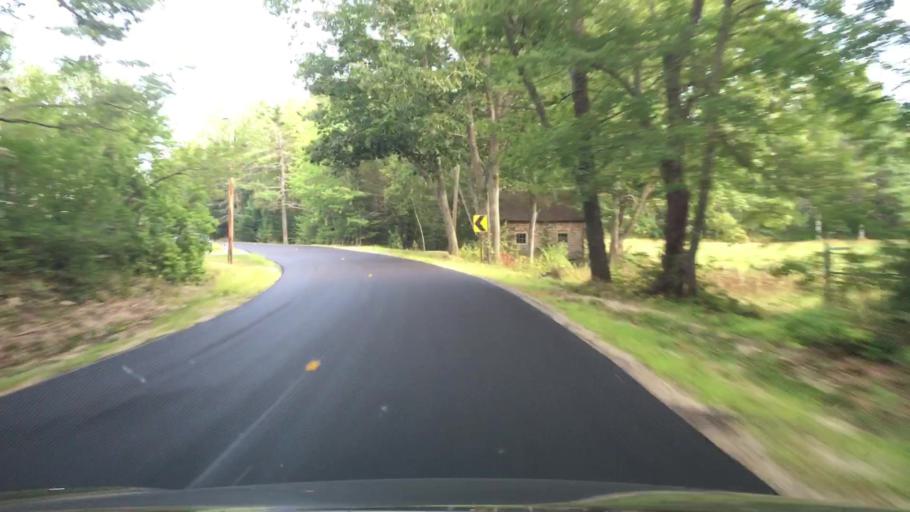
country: US
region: Maine
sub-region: Hancock County
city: Surry
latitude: 44.5176
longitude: -68.6067
